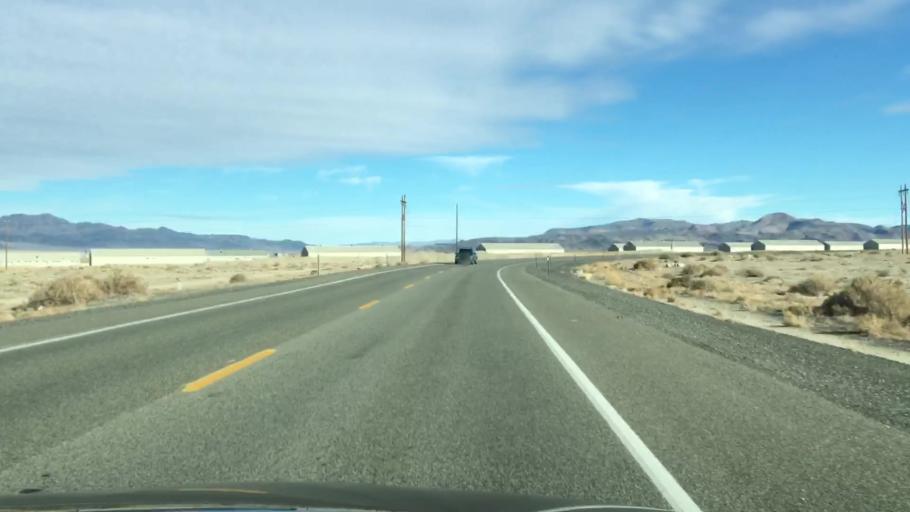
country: US
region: Nevada
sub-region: Mineral County
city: Hawthorne
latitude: 38.5336
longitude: -118.6152
